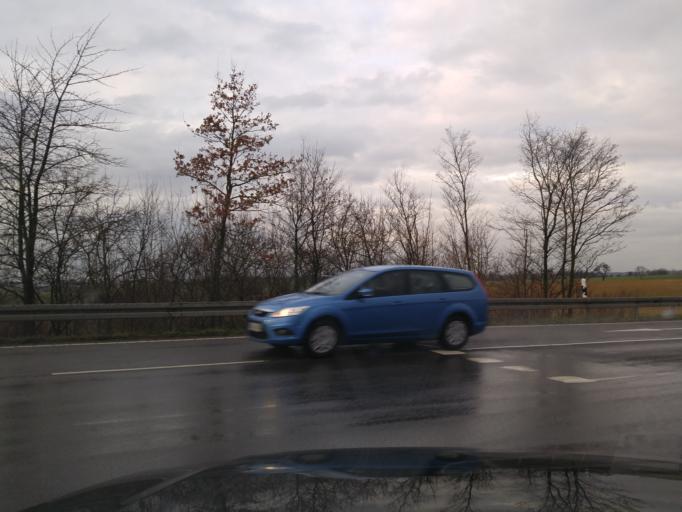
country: DE
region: Baden-Wuerttemberg
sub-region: Regierungsbezirk Stuttgart
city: Waldenburg
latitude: 49.2042
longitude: 9.6559
